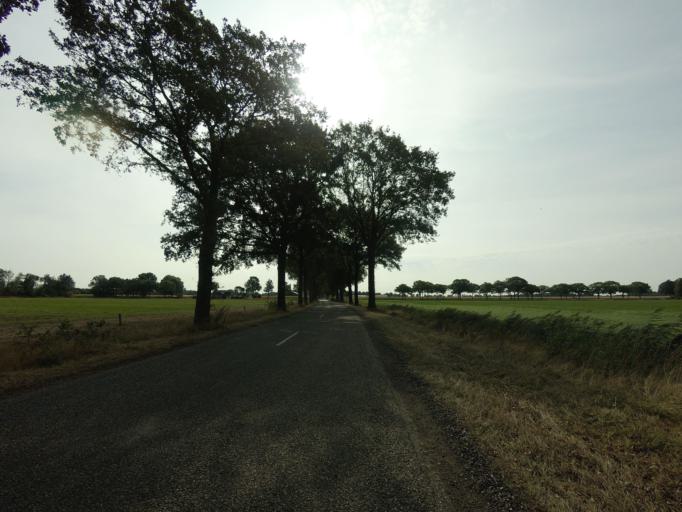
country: NL
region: North Brabant
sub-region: Gemeente Sint Anthonis
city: Sint Anthonis
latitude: 51.5881
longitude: 5.8464
